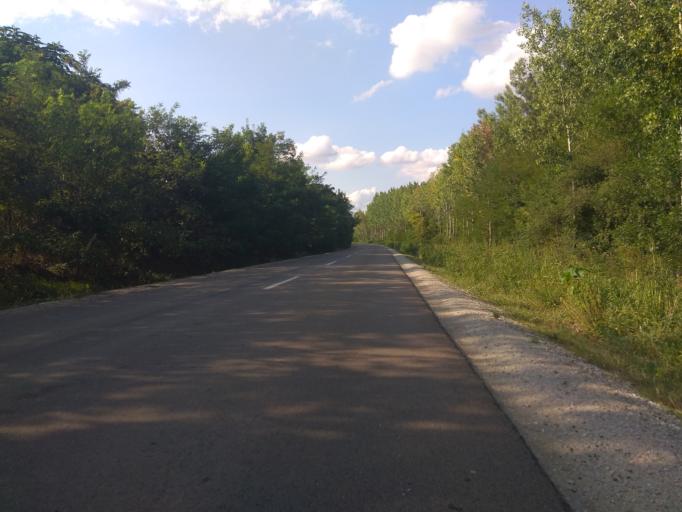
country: HU
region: Borsod-Abauj-Zemplen
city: Hejobaba
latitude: 47.8876
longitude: 20.8970
